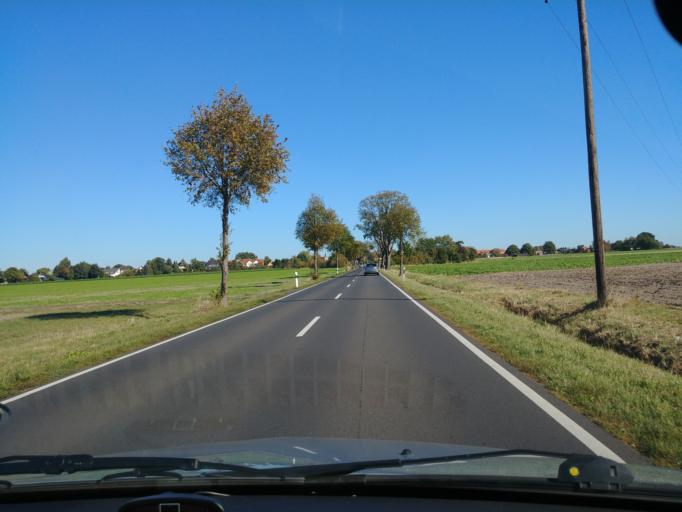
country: DE
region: Lower Saxony
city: Leiferde
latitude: 52.4299
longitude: 10.4314
